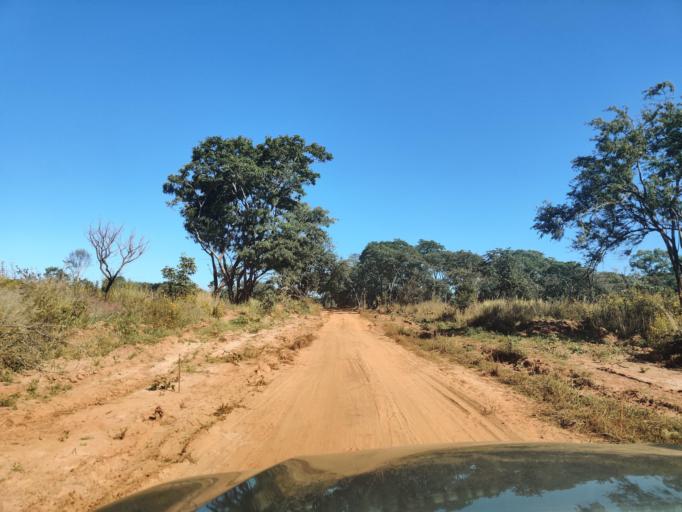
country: ZM
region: Central
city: Mkushi
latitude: -13.5264
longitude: 28.9109
